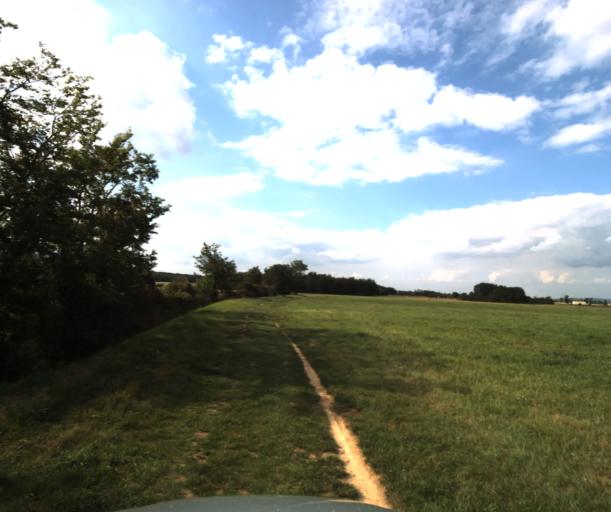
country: FR
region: Midi-Pyrenees
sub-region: Departement de la Haute-Garonne
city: Eaunes
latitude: 43.4405
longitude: 1.3585
